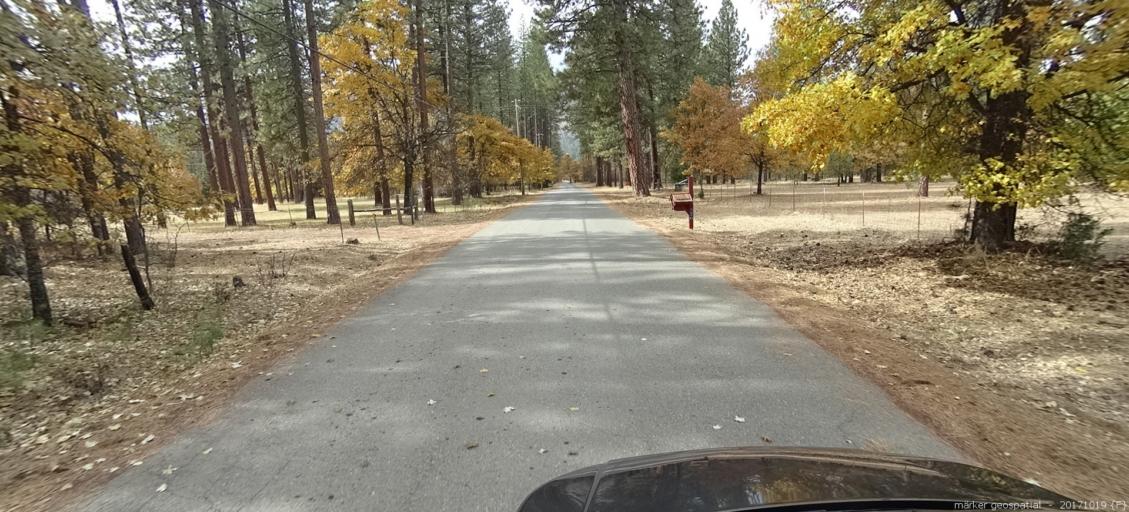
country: US
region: California
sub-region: Shasta County
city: Burney
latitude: 41.0799
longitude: -121.5280
